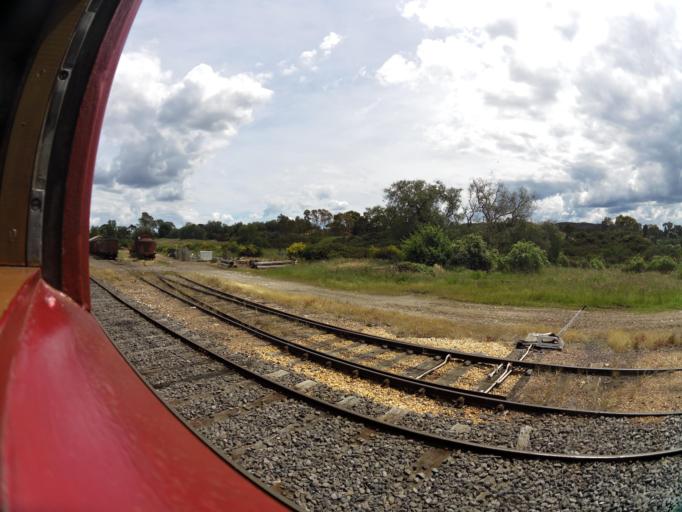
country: AU
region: Victoria
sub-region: Mount Alexander
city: Castlemaine
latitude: -36.9924
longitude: 144.0752
